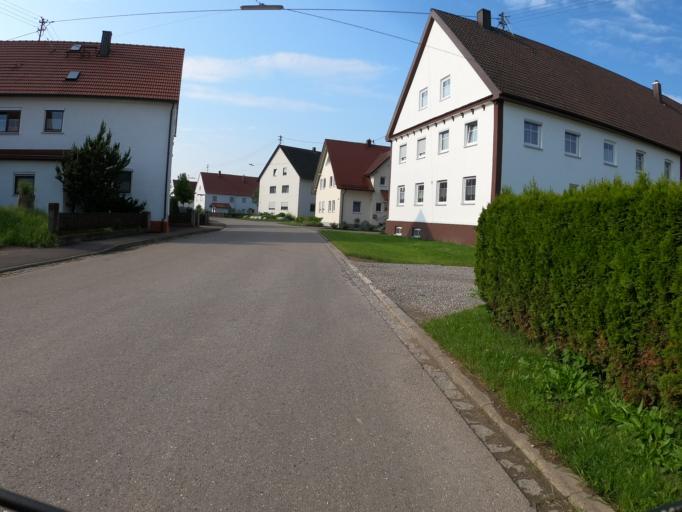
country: DE
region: Bavaria
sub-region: Swabia
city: Pfaffenhofen an der Roth
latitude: 48.3797
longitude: 10.1472
